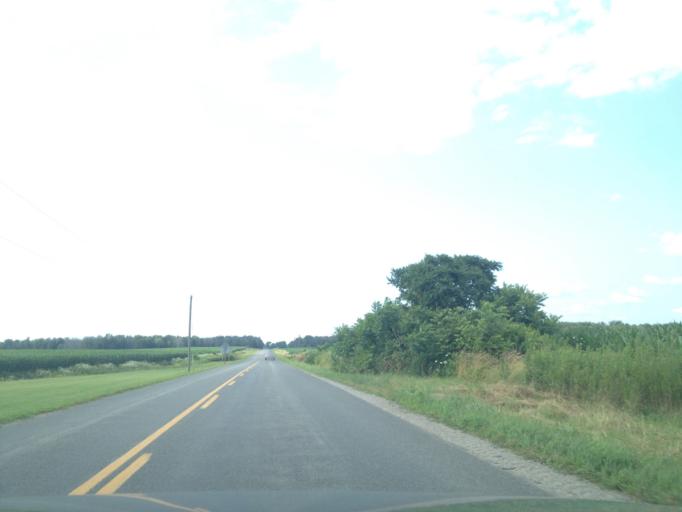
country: CA
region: Ontario
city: Aylmer
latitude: 42.6747
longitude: -80.8599
